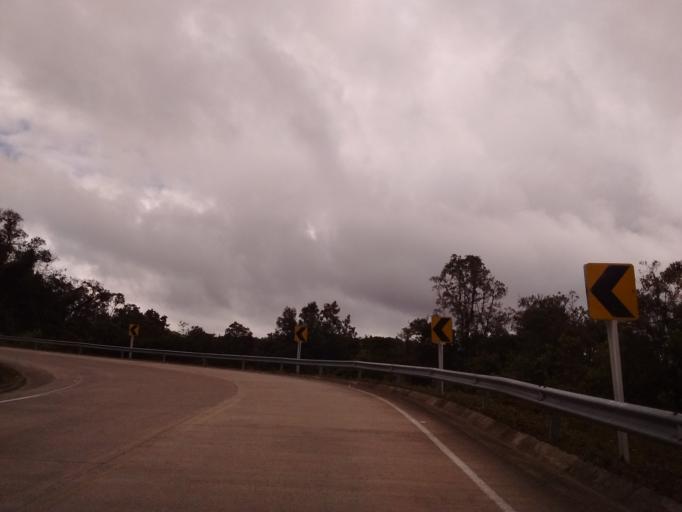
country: CO
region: Huila
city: Isnos
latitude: 2.0486
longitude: -76.2944
